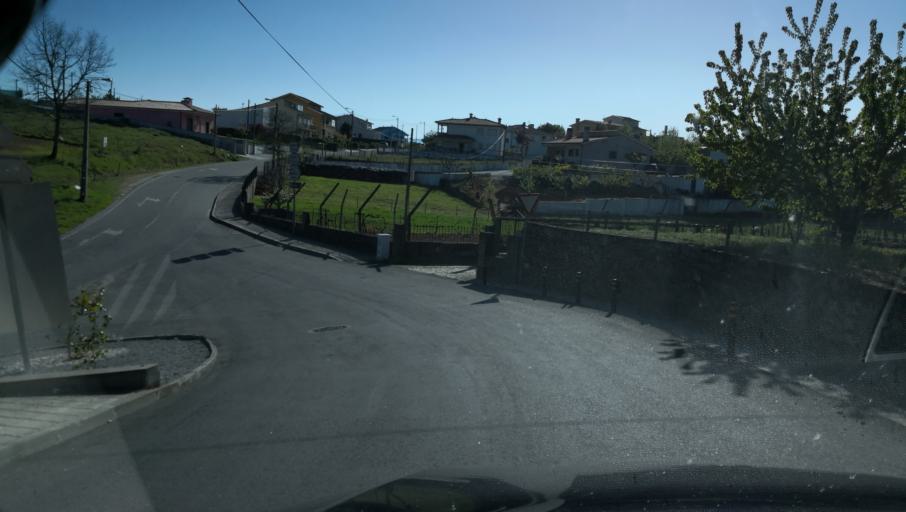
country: PT
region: Vila Real
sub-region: Vila Real
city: Vila Real
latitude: 41.2805
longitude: -7.6866
